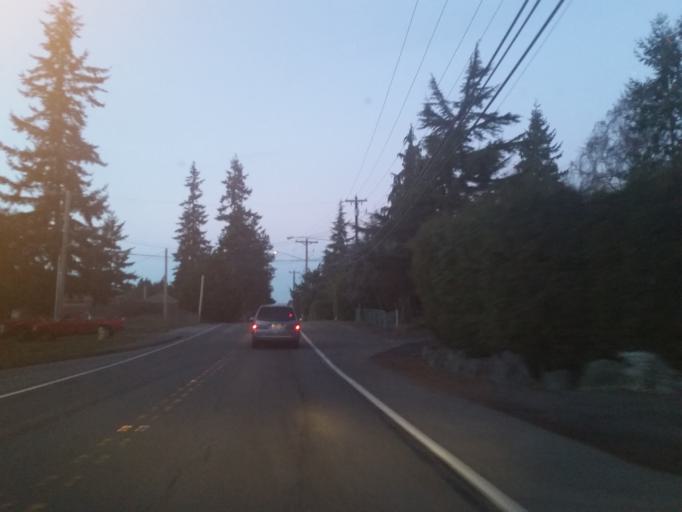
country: US
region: Washington
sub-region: Snohomish County
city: Lynnwood
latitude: 47.8432
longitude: -122.3036
